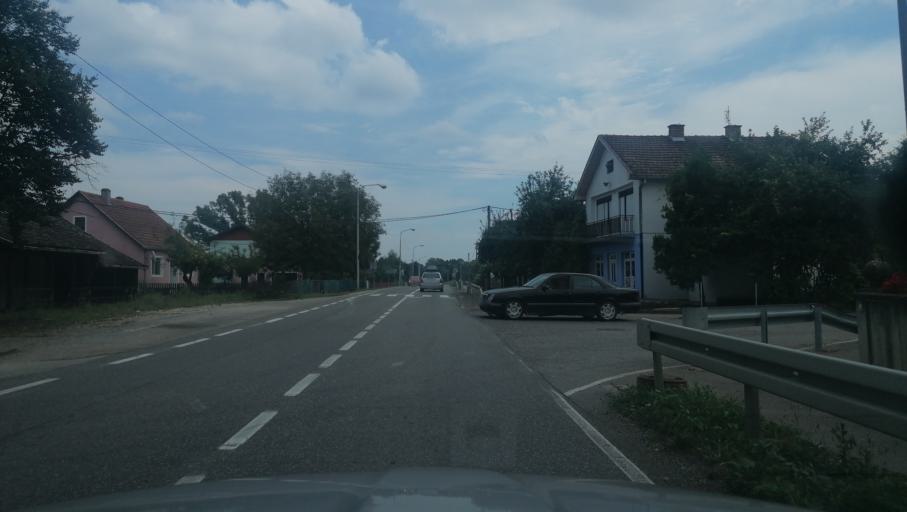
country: BA
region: Republika Srpska
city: Obudovac
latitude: 44.9526
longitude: 18.6454
